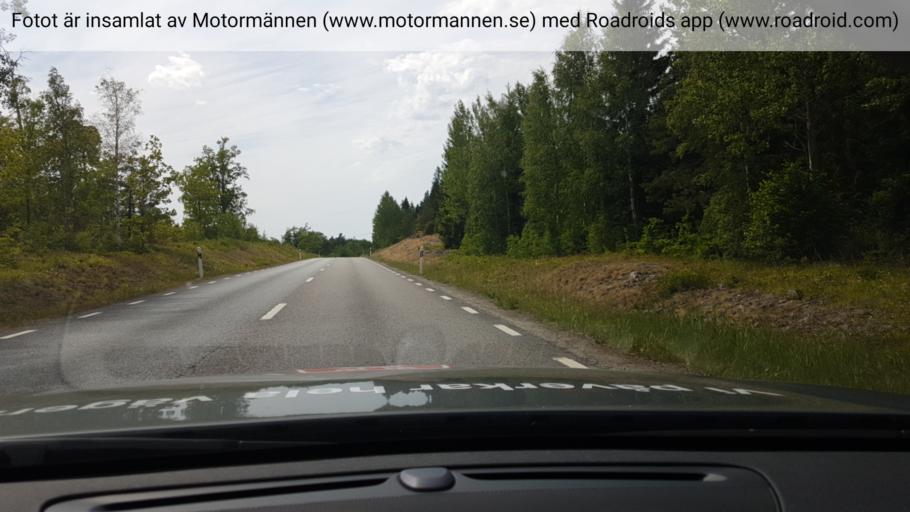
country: SE
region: Uppsala
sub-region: Osthammars Kommun
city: Marieberg
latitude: 60.1646
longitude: 18.4710
